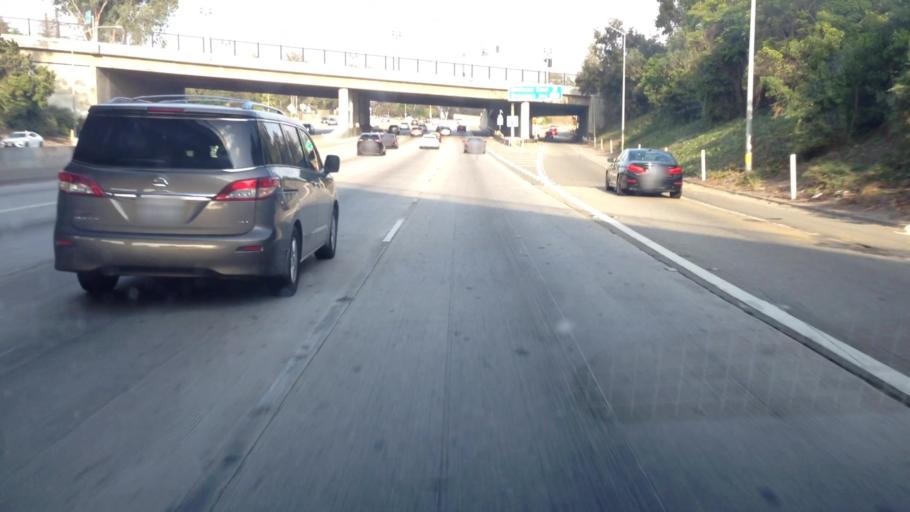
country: US
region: California
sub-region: Los Angeles County
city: Century City
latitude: 34.0316
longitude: -118.4187
